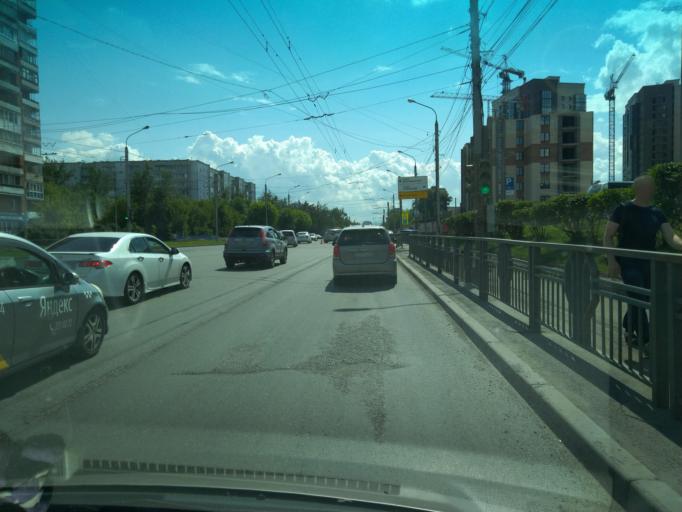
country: RU
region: Krasnoyarskiy
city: Solnechnyy
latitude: 56.0545
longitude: 92.9412
